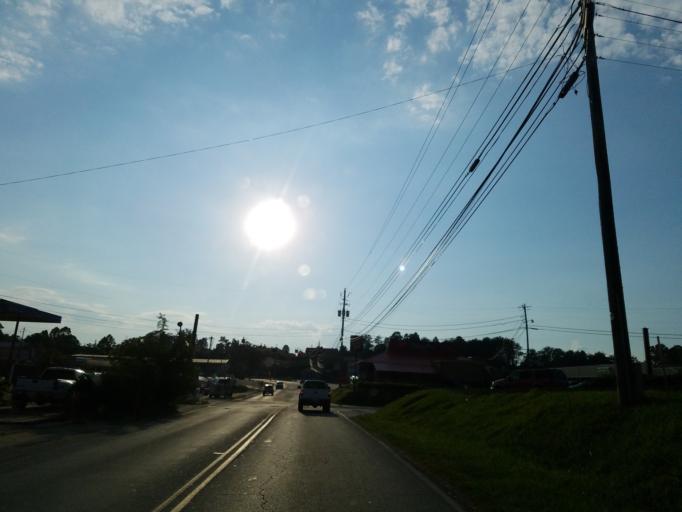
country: US
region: Georgia
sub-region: Fannin County
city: Blue Ridge
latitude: 34.8731
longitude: -84.3095
